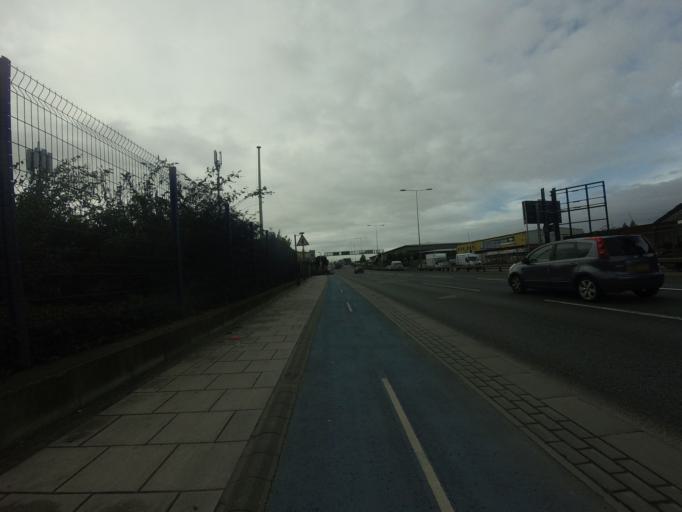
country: GB
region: England
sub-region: Greater London
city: Barking
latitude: 51.5287
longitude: 0.0853
